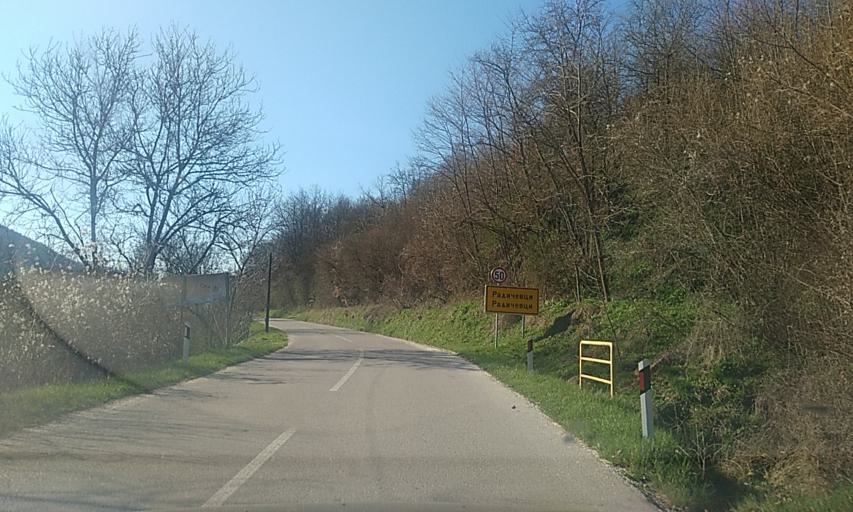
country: RS
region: Central Serbia
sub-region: Pcinjski Okrug
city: Bosilegrad
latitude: 42.4698
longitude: 22.4821
